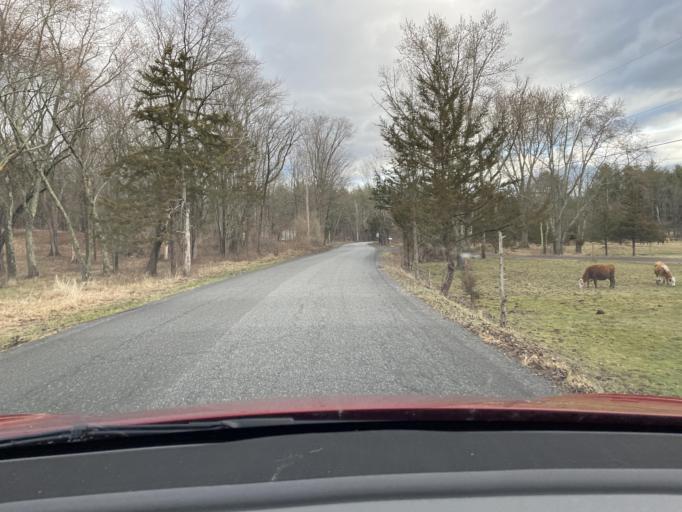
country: US
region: New York
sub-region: Ulster County
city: Manorville
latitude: 42.0770
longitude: -74.0412
